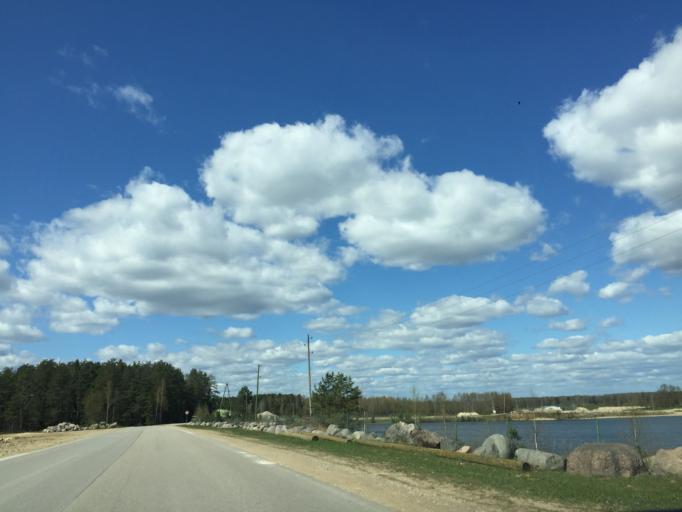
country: LV
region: Vilanu
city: Vilani
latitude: 56.5731
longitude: 27.0451
